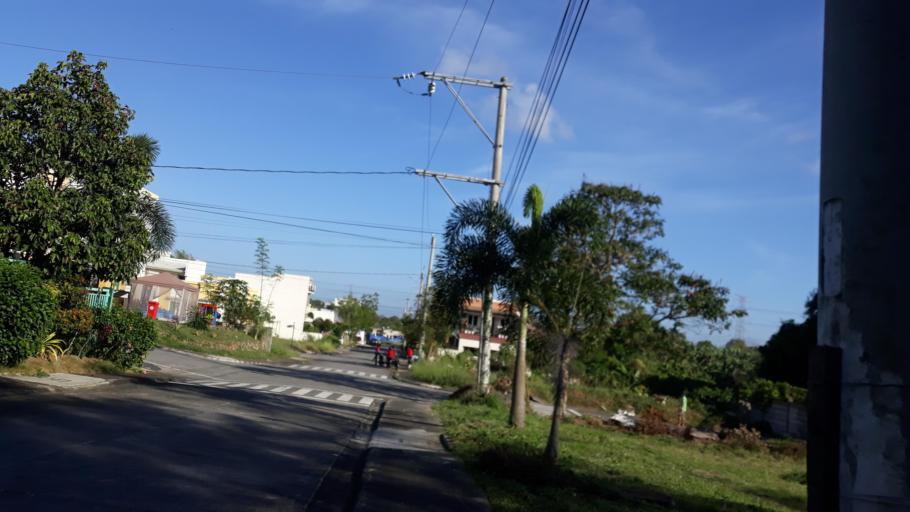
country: PH
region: Calabarzon
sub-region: Province of Cavite
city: Biga
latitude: 14.2777
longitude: 120.9742
